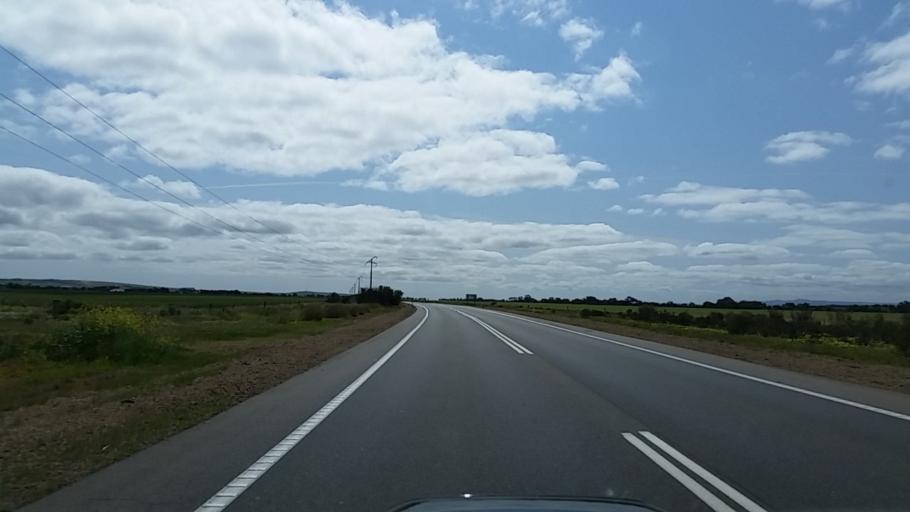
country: AU
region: South Australia
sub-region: Port Pirie City and Dists
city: Crystal Brook
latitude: -33.4909
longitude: 138.1797
